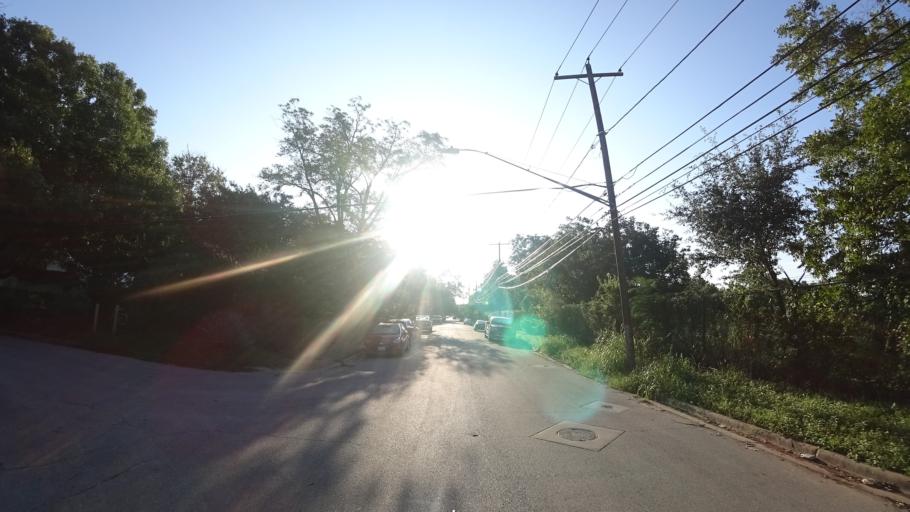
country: US
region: Texas
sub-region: Travis County
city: Austin
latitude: 30.2546
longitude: -97.7326
